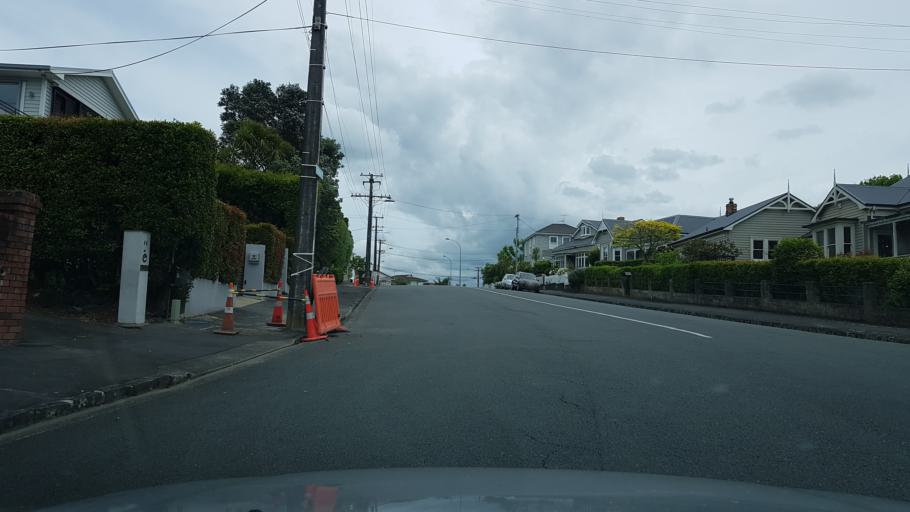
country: NZ
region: Auckland
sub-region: Auckland
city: North Shore
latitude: -36.8190
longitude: 174.7353
